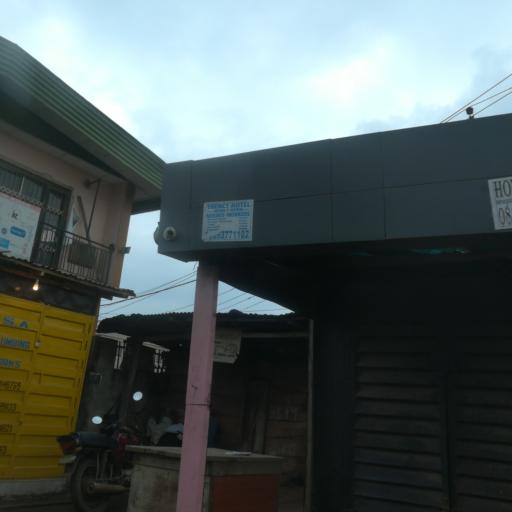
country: NG
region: Lagos
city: Agege
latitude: 6.5976
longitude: 3.2936
